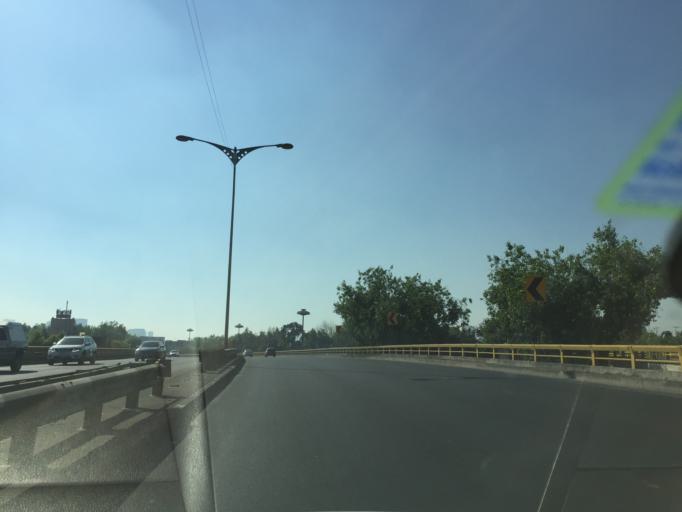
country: MX
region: Mexico City
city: Azcapotzalco
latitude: 19.4626
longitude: -99.1902
